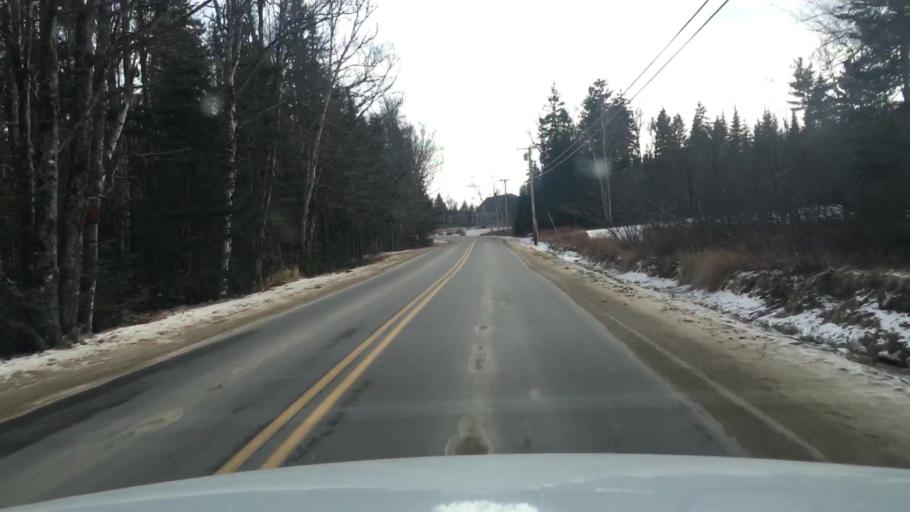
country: US
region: Maine
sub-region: Washington County
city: Jonesport
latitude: 44.6111
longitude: -67.6021
